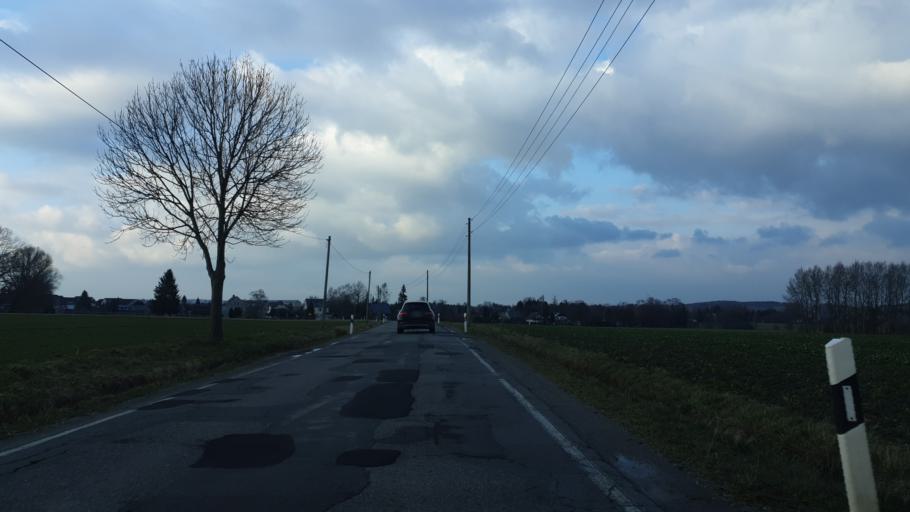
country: DE
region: Saxony
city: Niederdorf
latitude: 50.7599
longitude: 12.8045
